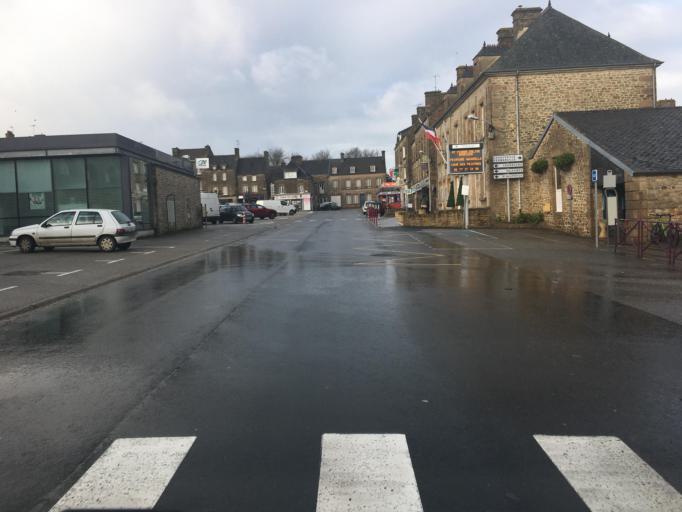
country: FR
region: Lower Normandy
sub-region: Departement de la Manche
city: Saint-Pierre-Eglise
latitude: 49.6683
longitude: -1.4040
